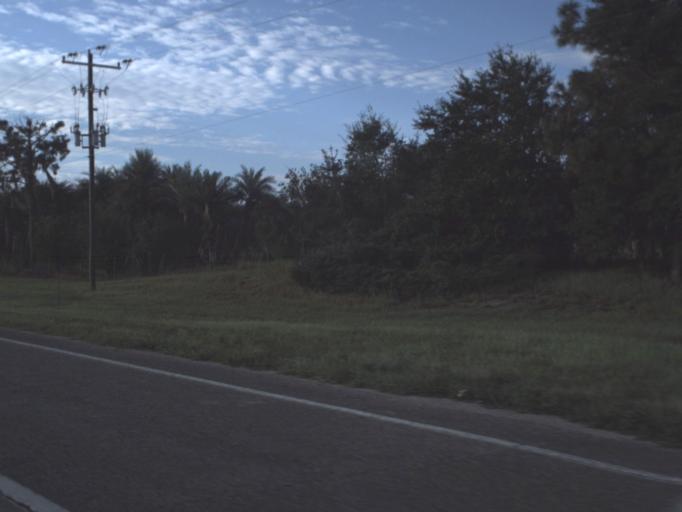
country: US
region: Florida
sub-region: Highlands County
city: Lake Placid
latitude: 27.3753
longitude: -81.4031
